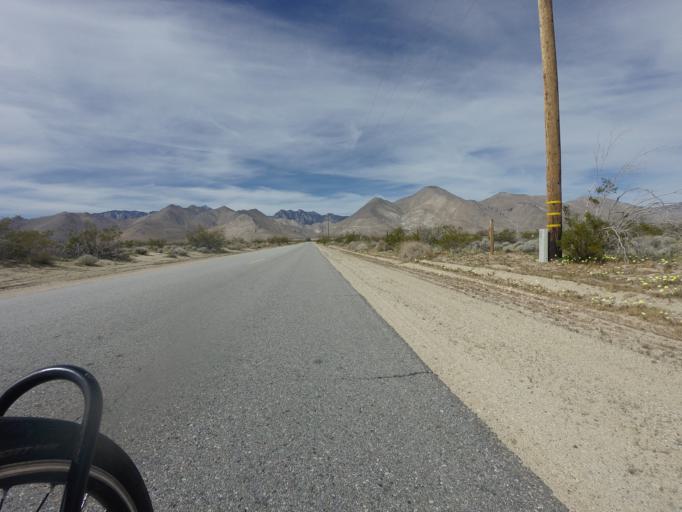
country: US
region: California
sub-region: Kern County
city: Inyokern
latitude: 35.7764
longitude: -117.8662
